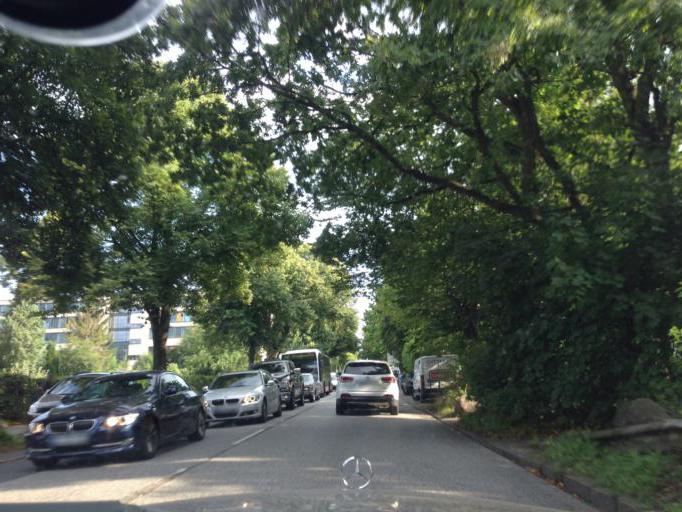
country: DE
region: Hamburg
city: Steilshoop
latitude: 53.5957
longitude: 10.0729
